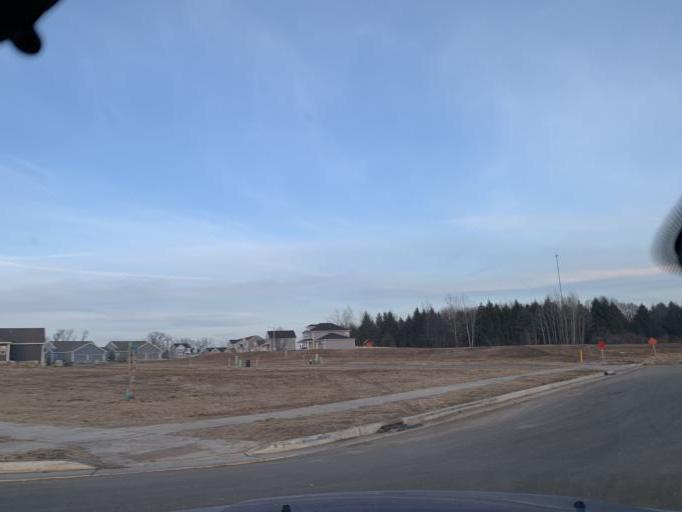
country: US
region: Wisconsin
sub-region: Dane County
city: Verona
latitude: 43.0504
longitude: -89.5649
